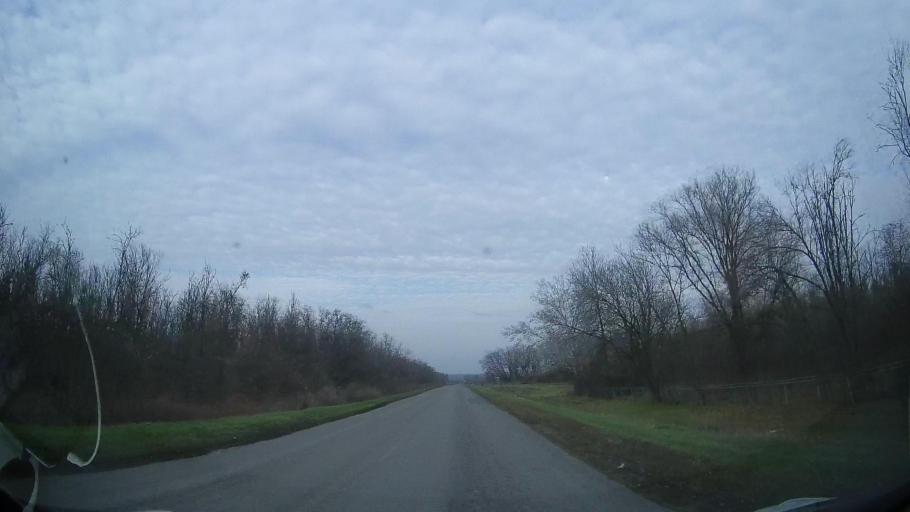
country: RU
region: Rostov
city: Zernograd
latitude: 46.8766
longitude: 40.3356
